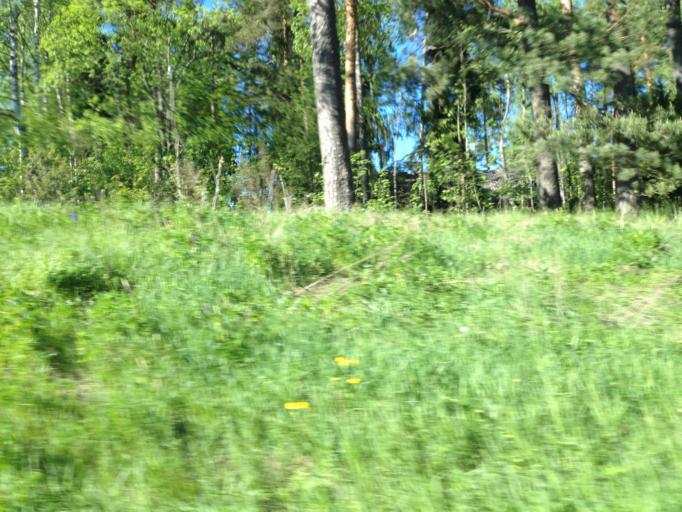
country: FI
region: Uusimaa
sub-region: Helsinki
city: Espoo
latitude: 60.2431
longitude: 24.5814
